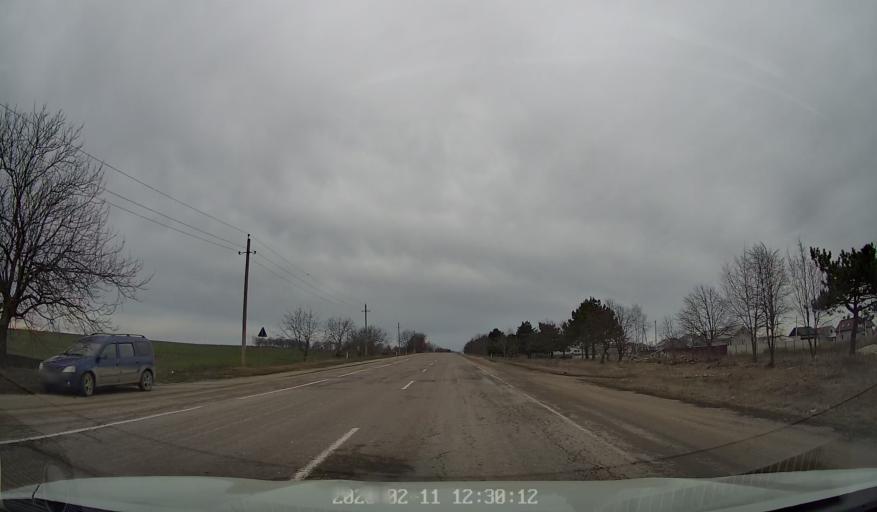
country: MD
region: Raionul Edinet
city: Edinet
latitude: 48.1608
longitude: 27.2854
